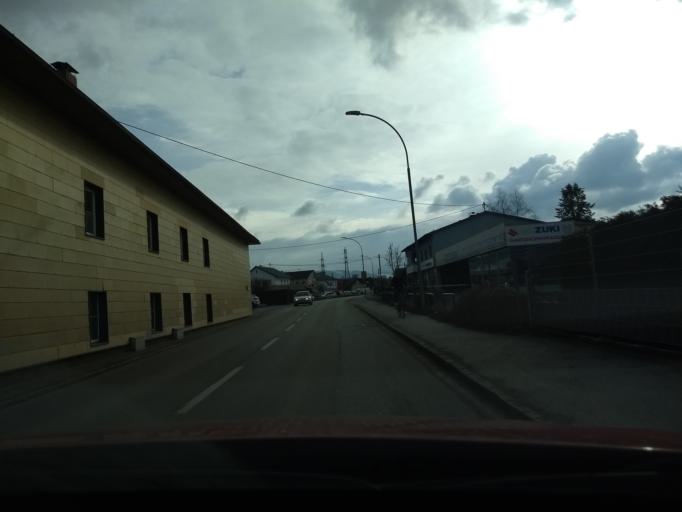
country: AT
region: Lower Austria
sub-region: Politischer Bezirk Amstetten
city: Haidershofen
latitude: 48.0721
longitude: 14.4240
